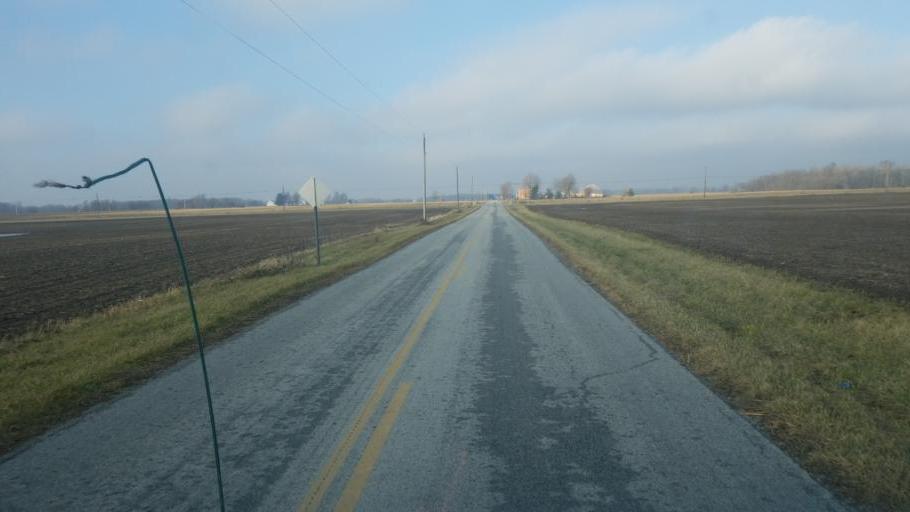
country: US
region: Ohio
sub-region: Hardin County
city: Kenton
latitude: 40.7012
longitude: -83.5923
